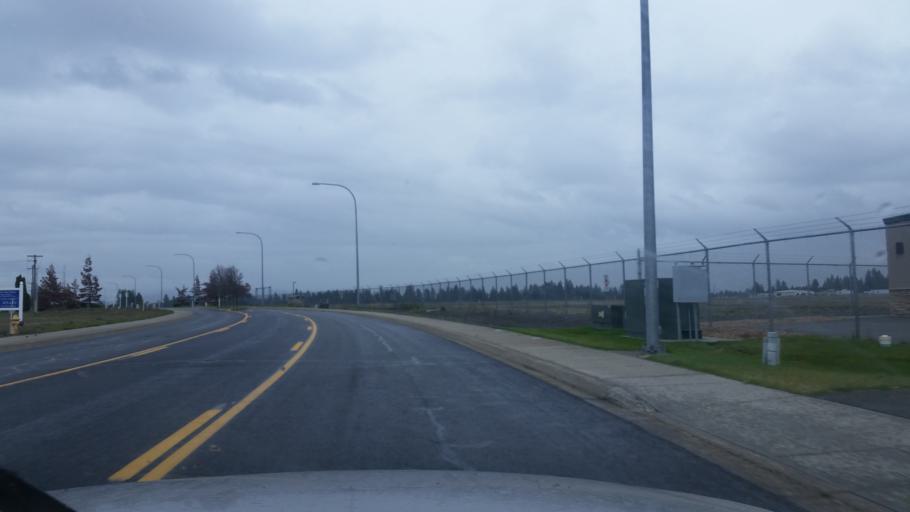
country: US
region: Washington
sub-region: Spokane County
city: Airway Heights
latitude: 47.6192
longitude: -117.5211
